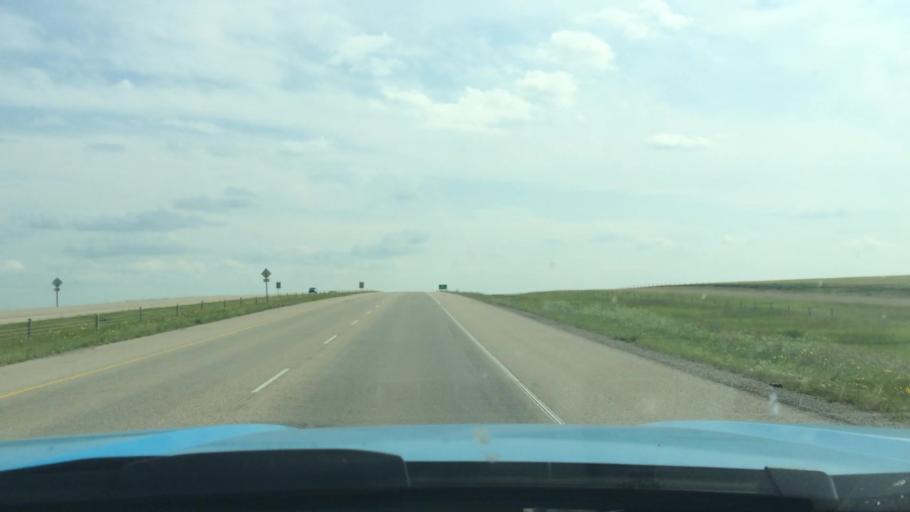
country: CA
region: Alberta
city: Carstairs
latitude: 51.5758
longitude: -114.0254
